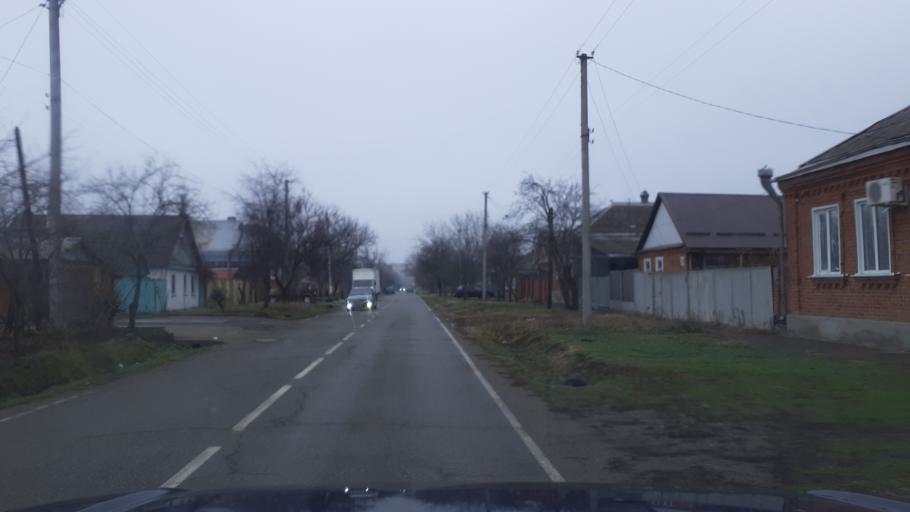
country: RU
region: Adygeya
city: Maykop
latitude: 44.6192
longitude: 40.0758
